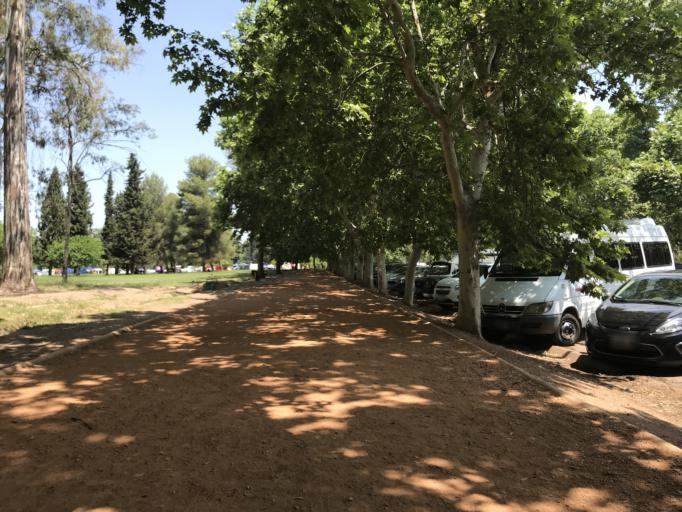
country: AR
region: Mendoza
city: Mendoza
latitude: -32.8951
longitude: -68.8673
